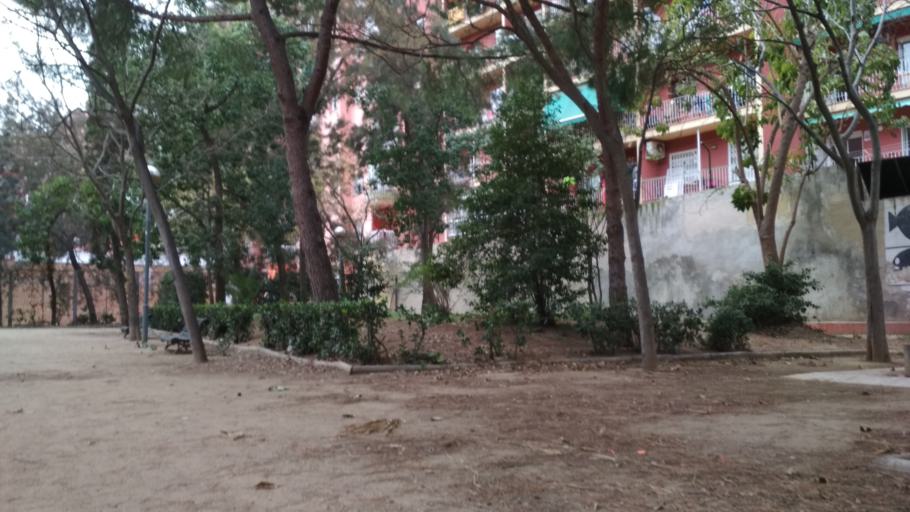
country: ES
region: Catalonia
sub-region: Provincia de Barcelona
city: Sants-Montjuic
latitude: 41.3625
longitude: 2.1385
